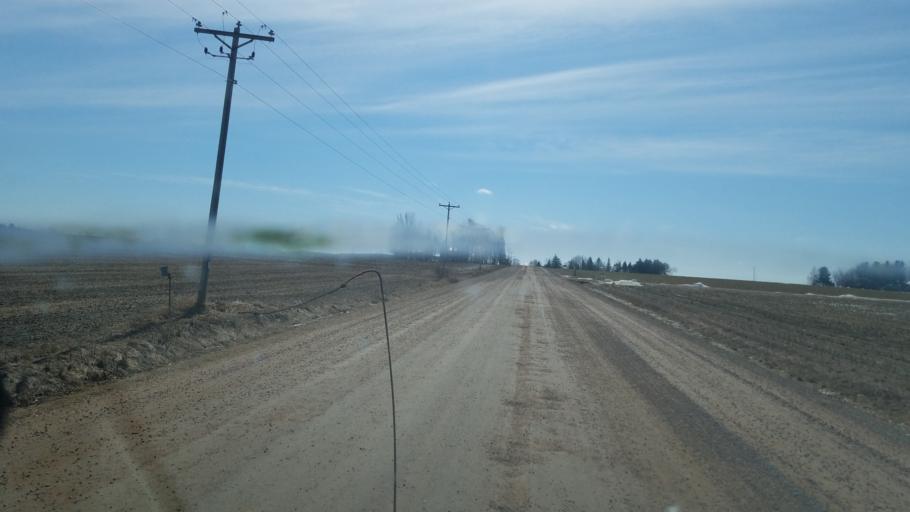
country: US
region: Wisconsin
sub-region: Clark County
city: Loyal
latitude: 44.6084
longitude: -90.4565
